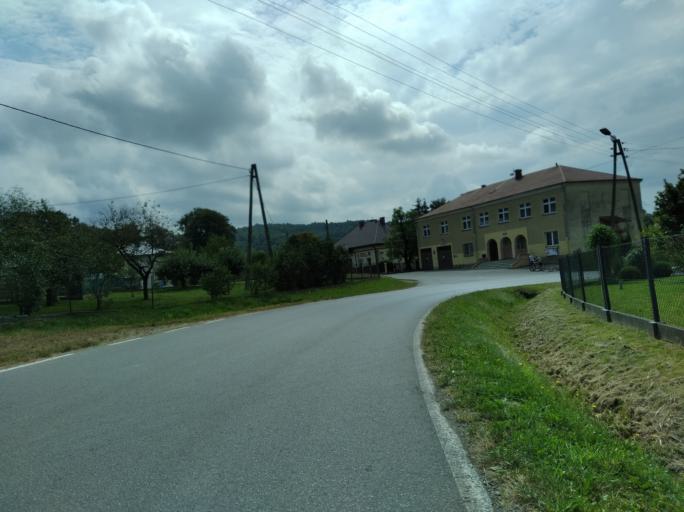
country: PL
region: Subcarpathian Voivodeship
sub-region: Powiat krosnienski
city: Wojaszowka
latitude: 49.7888
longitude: 21.6916
